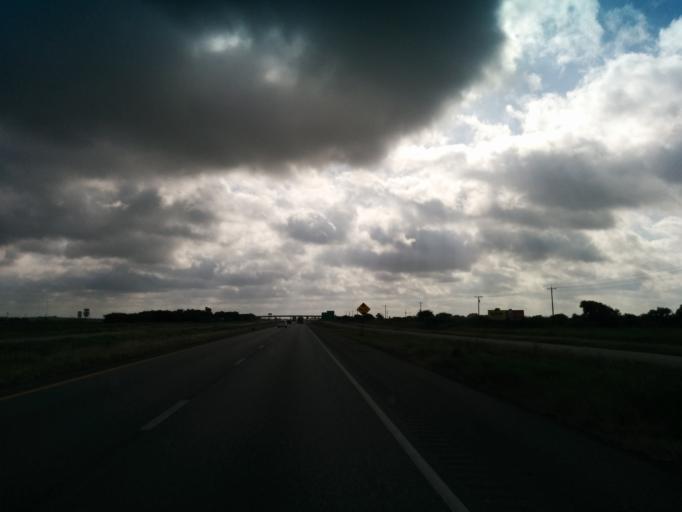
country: US
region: Texas
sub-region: Guadalupe County
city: Marion
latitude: 29.5162
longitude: -98.1460
